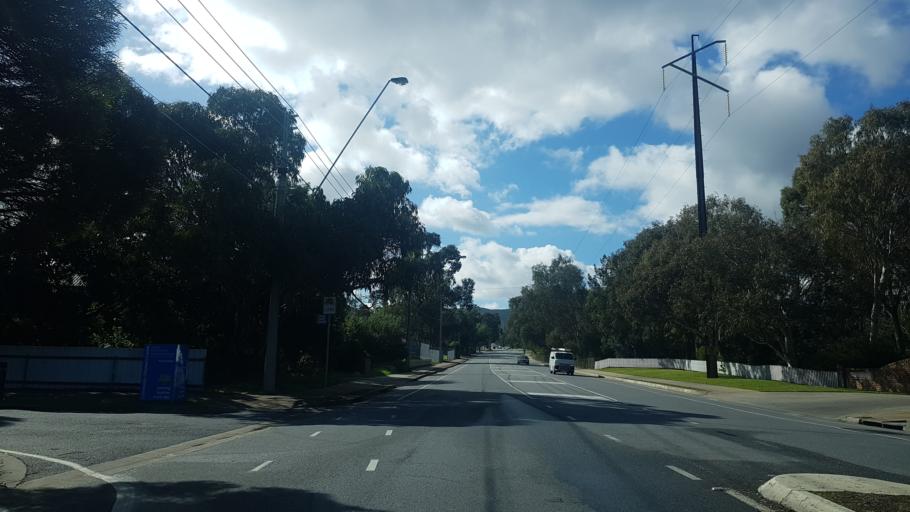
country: AU
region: South Australia
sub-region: Tea Tree Gully
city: Hope Valley
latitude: -34.8329
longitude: 138.6976
